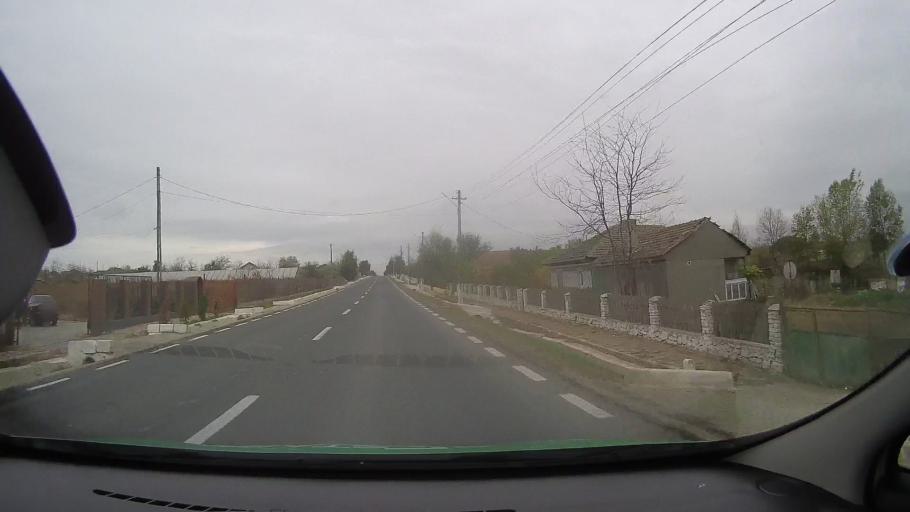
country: RO
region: Constanta
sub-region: Comuna Nicolae Balcescu
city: Dorobantu
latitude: 44.4122
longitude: 28.3214
